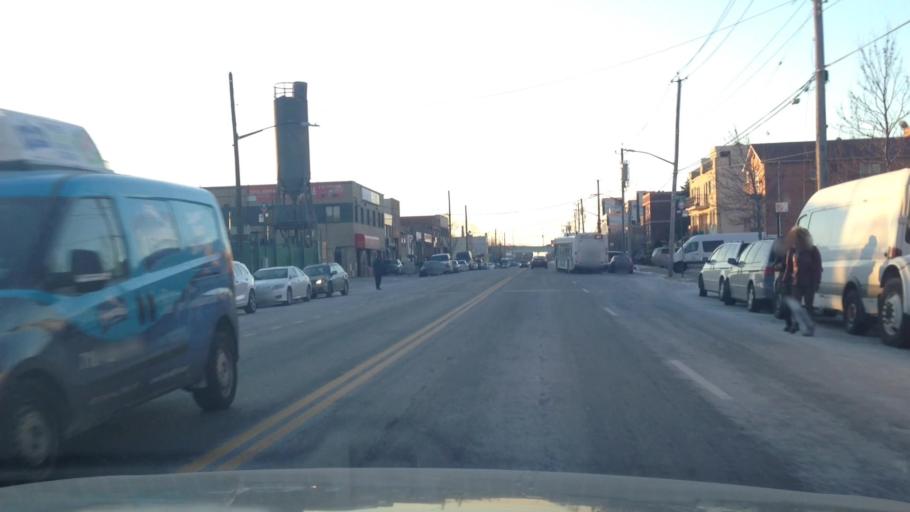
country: US
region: New York
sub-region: Kings County
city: Coney Island
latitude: 40.5869
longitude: -73.9834
